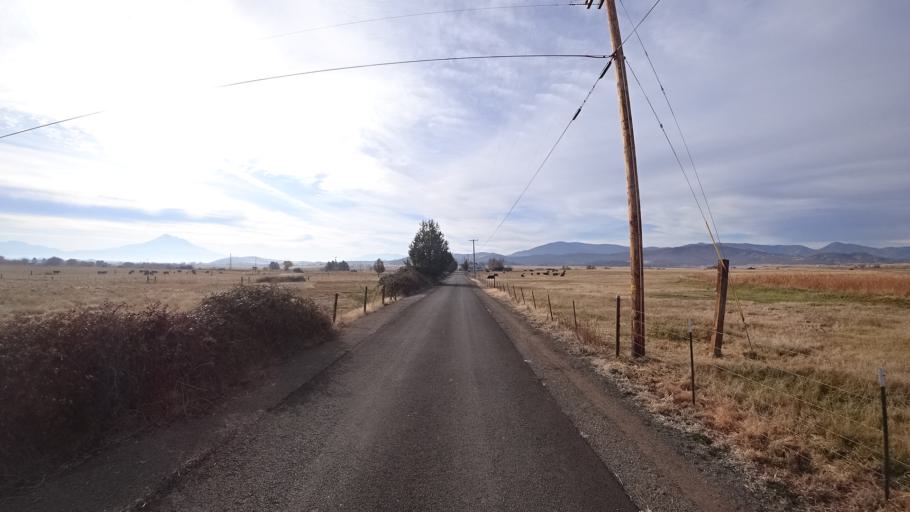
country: US
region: California
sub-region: Siskiyou County
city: Montague
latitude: 41.7277
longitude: -122.5786
